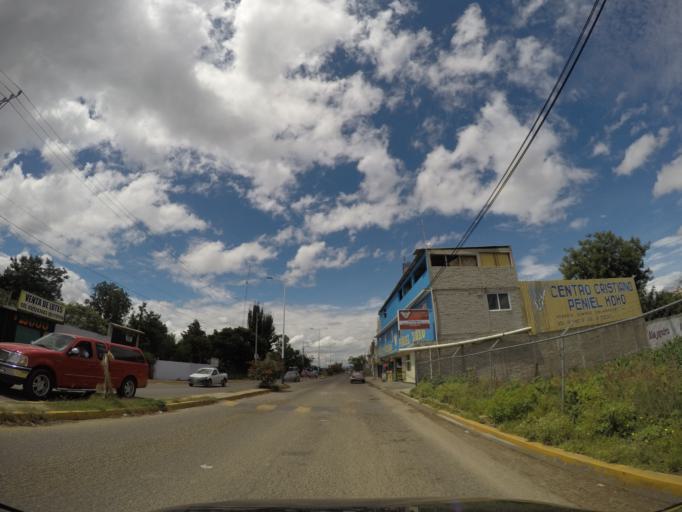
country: MX
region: Oaxaca
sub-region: Santa Cruz Xoxocotlan
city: San Isidro Monjas
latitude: 17.0117
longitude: -96.7352
